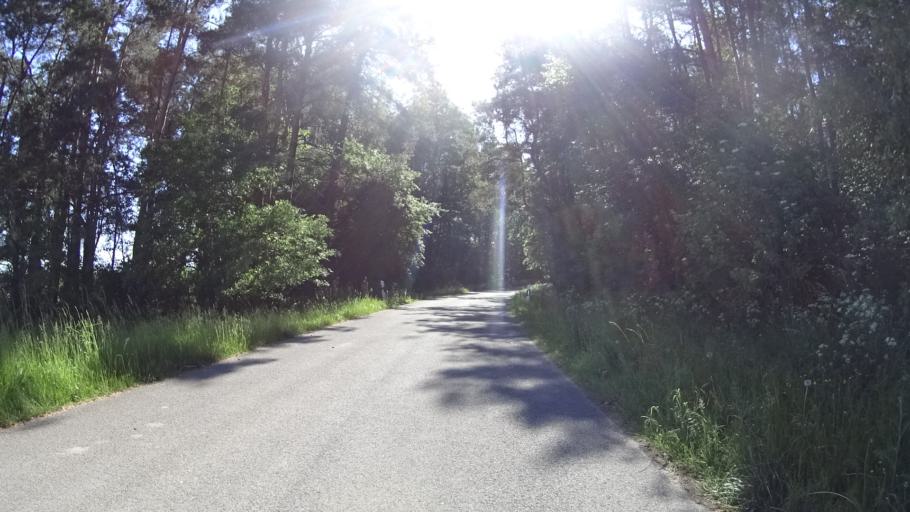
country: DE
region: Bavaria
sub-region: Regierungsbezirk Mittelfranken
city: Arberg
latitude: 49.1584
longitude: 10.5792
